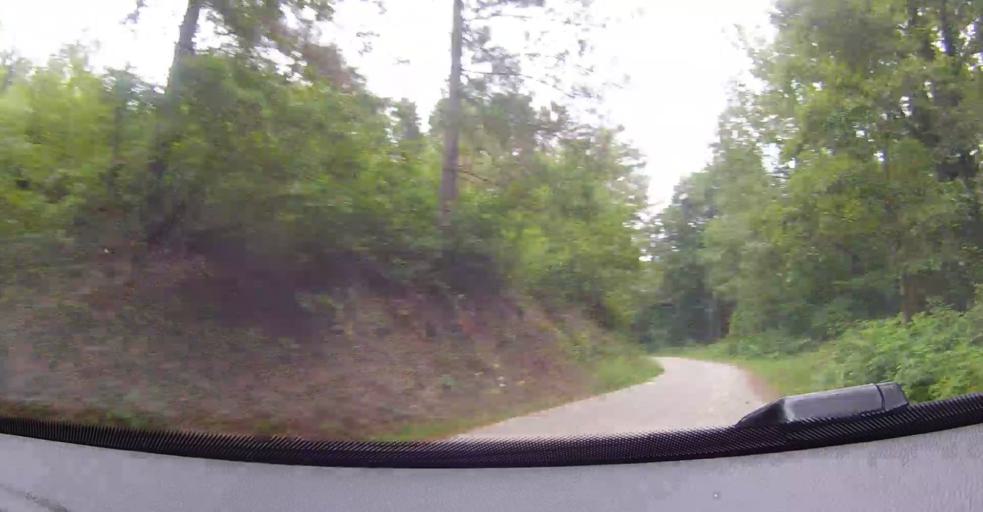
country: ES
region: Basque Country
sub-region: Bizkaia
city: Urrestieta
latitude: 43.2291
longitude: -3.1705
